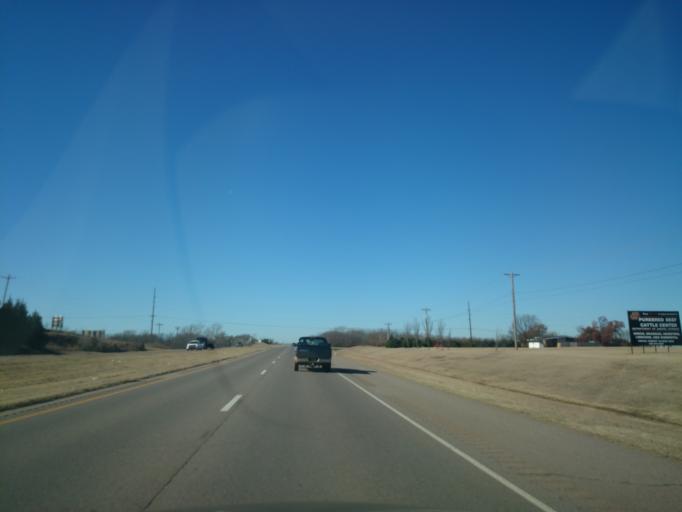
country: US
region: Oklahoma
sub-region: Payne County
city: Stillwater
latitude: 36.1161
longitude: -97.1380
